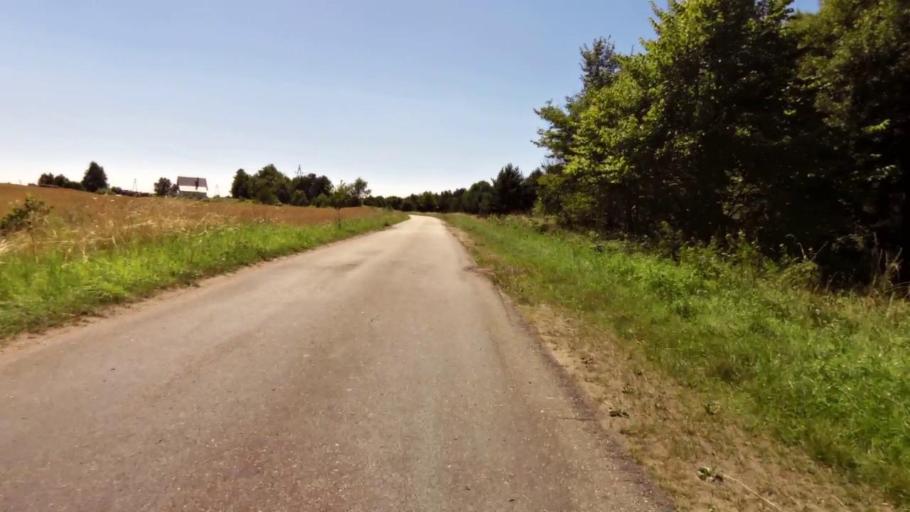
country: PL
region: West Pomeranian Voivodeship
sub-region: Powiat szczecinecki
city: Bialy Bor
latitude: 53.9321
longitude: 16.8525
